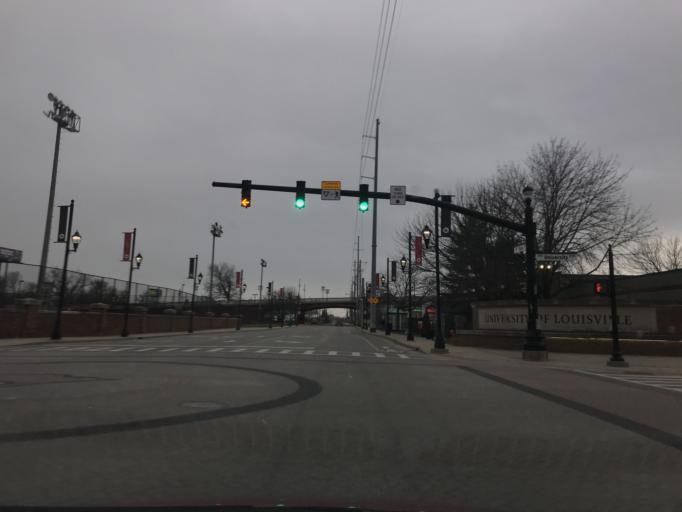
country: US
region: Kentucky
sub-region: Jefferson County
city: Audubon Park
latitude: 38.2148
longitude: -85.7552
